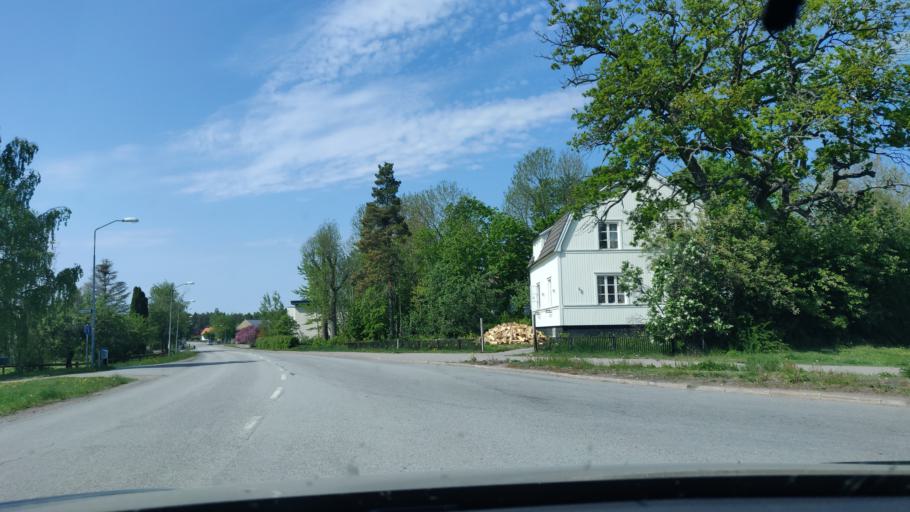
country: SE
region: Uppsala
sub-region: Heby Kommun
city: OEstervala
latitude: 60.1797
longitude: 17.1774
